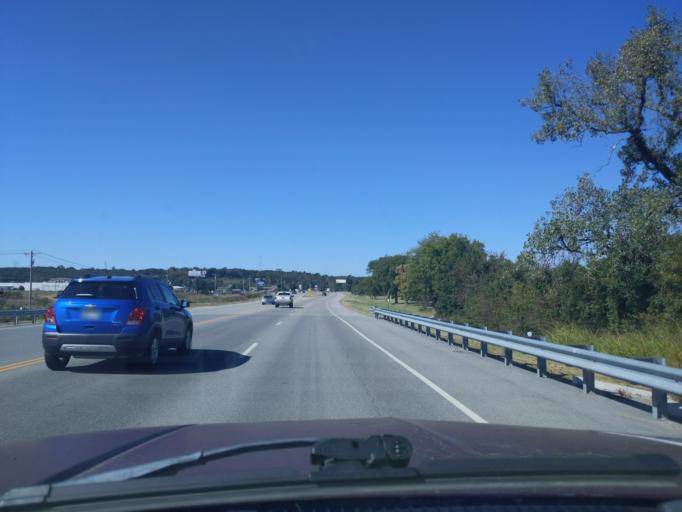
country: US
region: Oklahoma
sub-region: Creek County
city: Sapulpa
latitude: 35.9883
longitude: -96.1286
